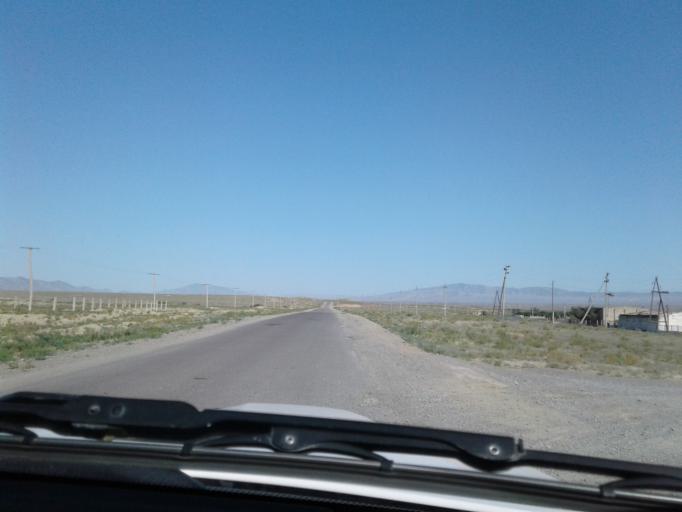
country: TM
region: Balkan
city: Magtymguly
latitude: 38.7050
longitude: 56.3474
